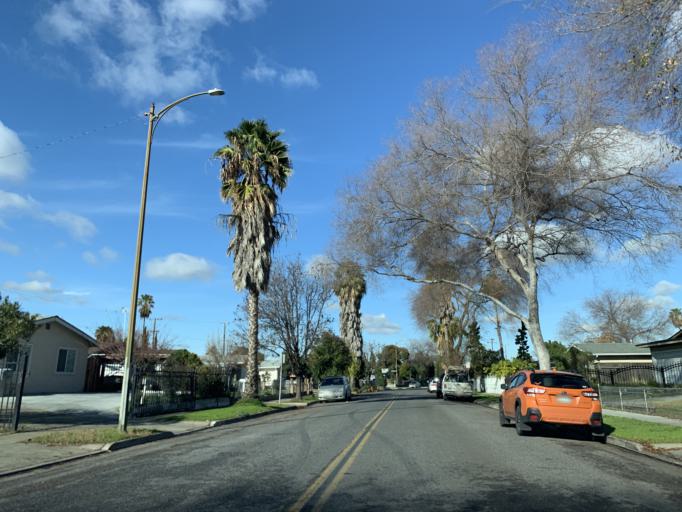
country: US
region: California
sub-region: Santa Clara County
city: Alum Rock
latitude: 37.3330
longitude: -121.8434
